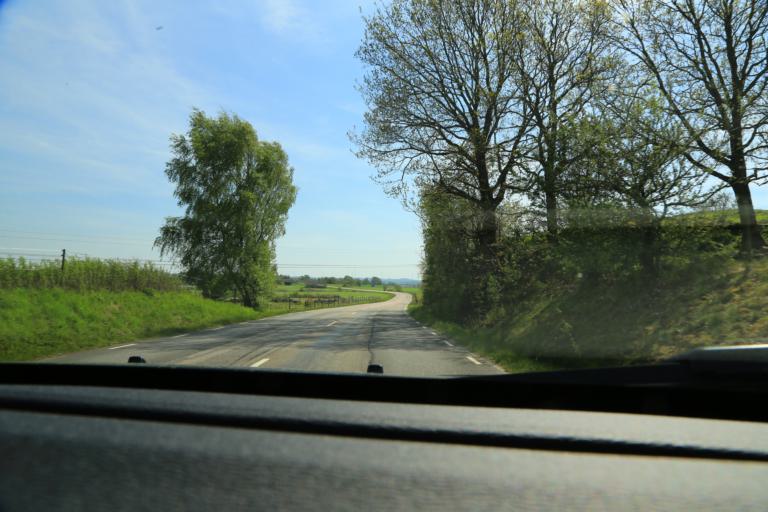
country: SE
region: Halland
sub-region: Varbergs Kommun
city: Varberg
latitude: 57.1378
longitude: 12.2983
